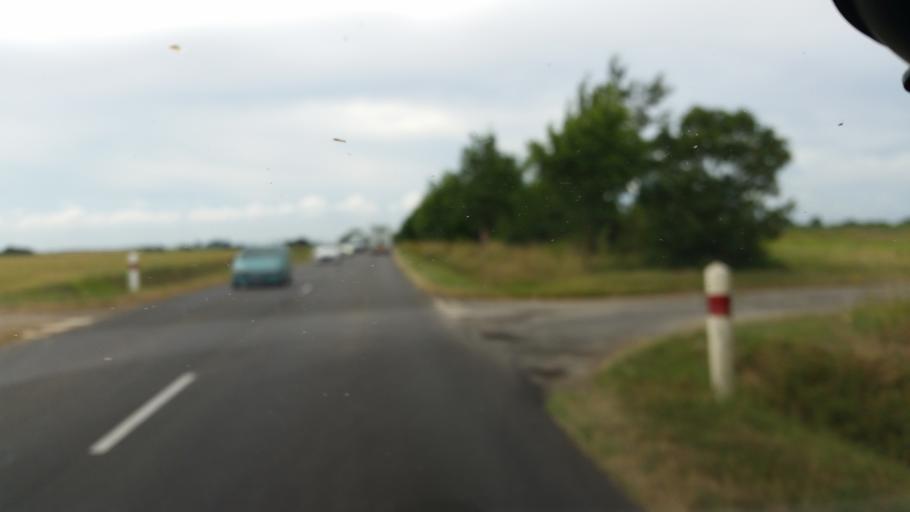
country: FR
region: Poitou-Charentes
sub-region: Departement de la Charente-Maritime
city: Surgeres
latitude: 46.1374
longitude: -0.7932
